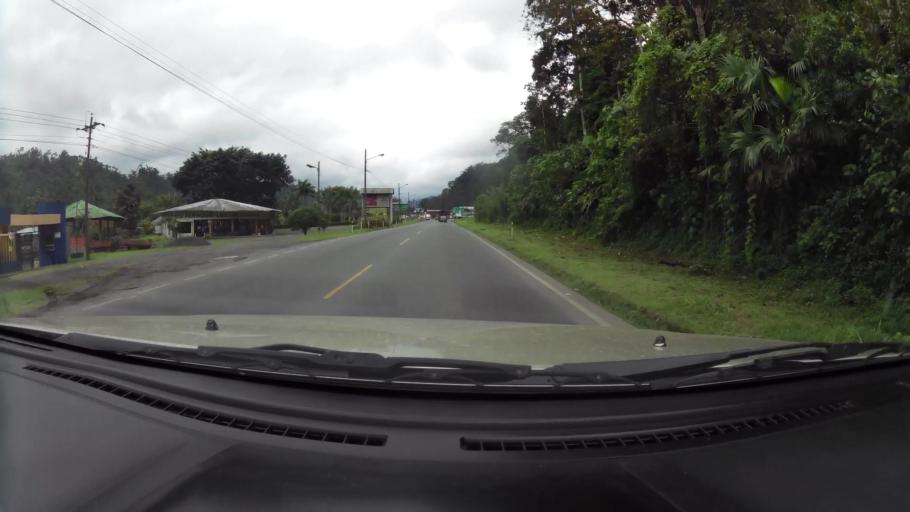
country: EC
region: Santo Domingo de los Tsachilas
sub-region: Canton Santo Domingo de los Colorados
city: Santo Domingo de los Colorados
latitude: -0.2727
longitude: -79.0804
